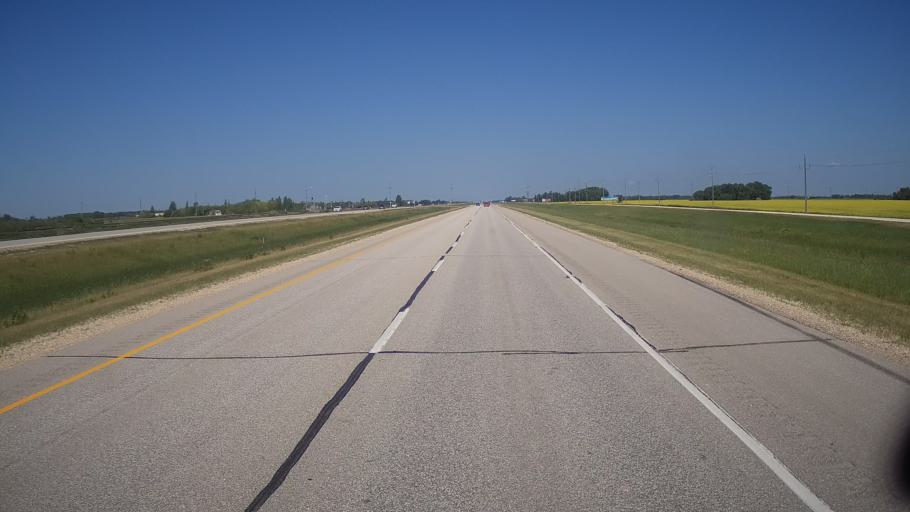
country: CA
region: Manitoba
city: Niverville
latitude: 49.7891
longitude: -96.8602
